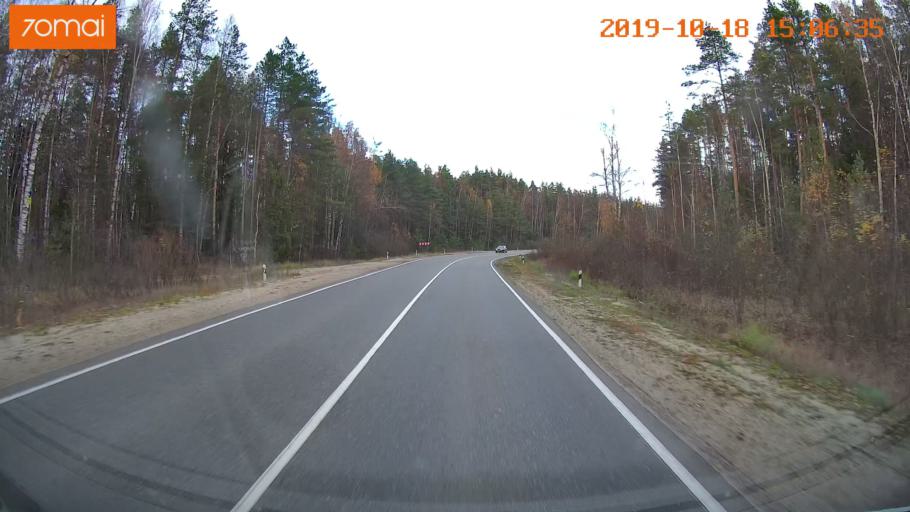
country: RU
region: Vladimir
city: Gus'-Khrustal'nyy
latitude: 55.5322
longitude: 40.5797
